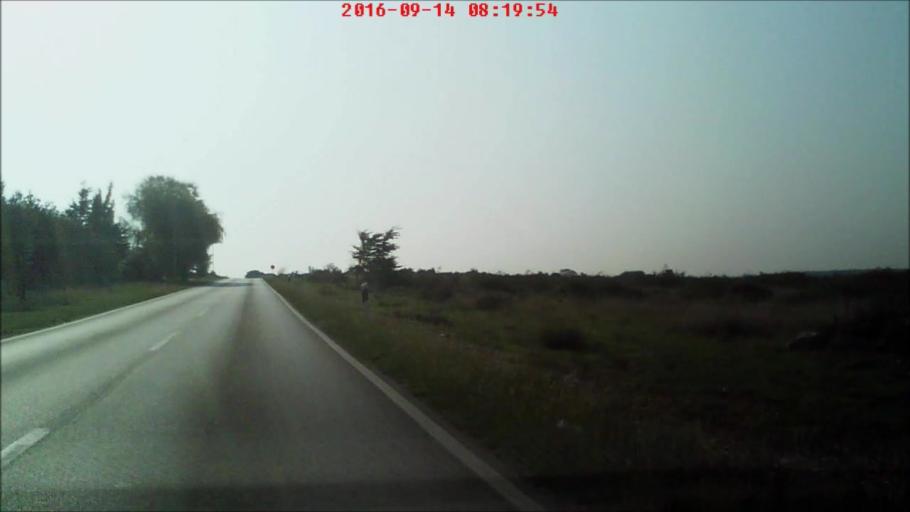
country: HR
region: Zadarska
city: Nin
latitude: 44.2295
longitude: 15.1952
